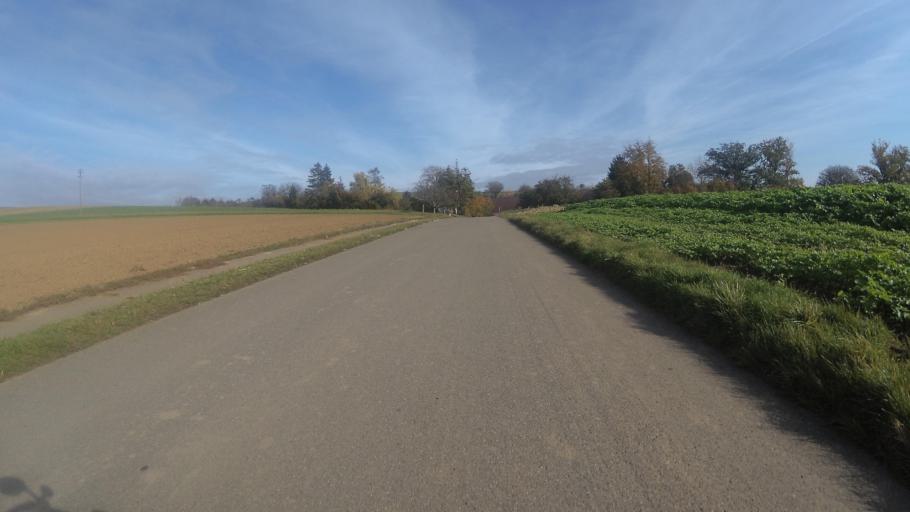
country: DE
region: Baden-Wuerttemberg
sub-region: Regierungsbezirk Stuttgart
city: Neudenau
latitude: 49.2636
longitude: 9.2825
